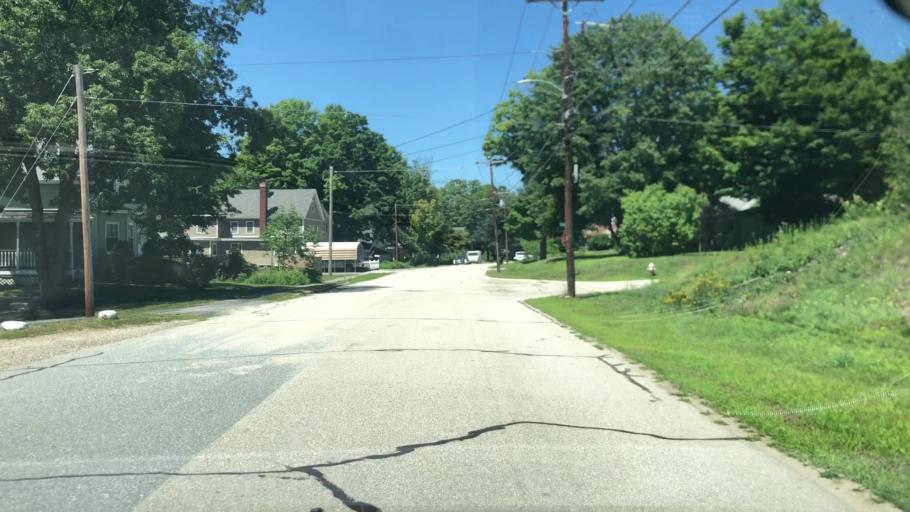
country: US
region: New Hampshire
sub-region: Hillsborough County
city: Milford
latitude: 42.8353
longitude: -71.6406
